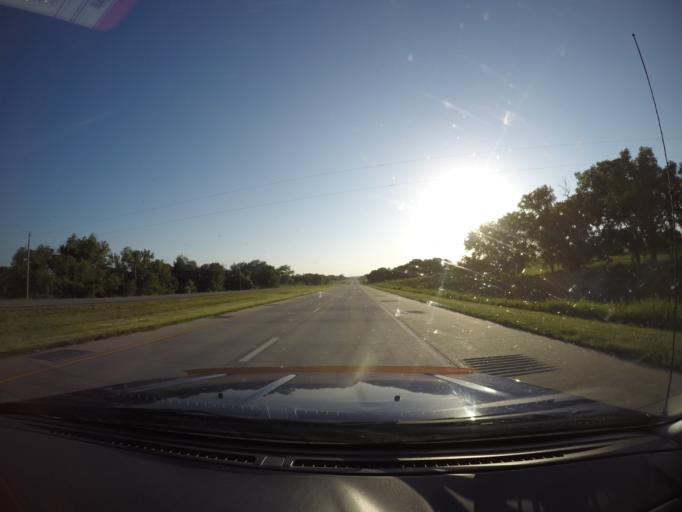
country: US
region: Kansas
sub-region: Riley County
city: Manhattan
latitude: 39.1986
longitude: -96.4588
